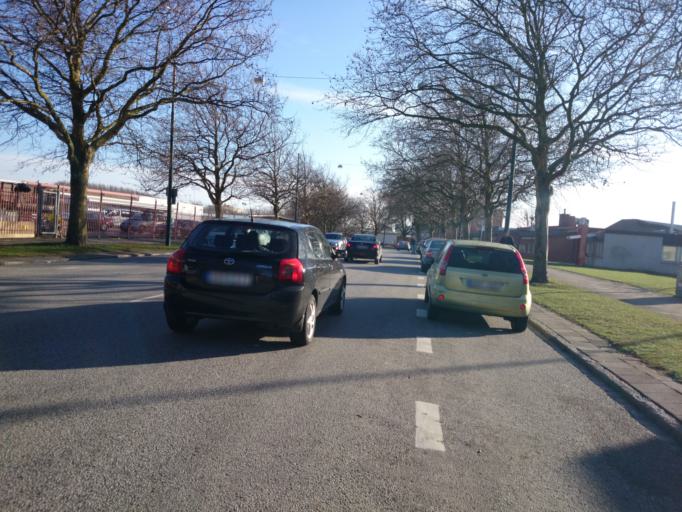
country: SE
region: Skane
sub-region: Malmo
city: Malmoe
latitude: 55.5960
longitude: 13.0368
